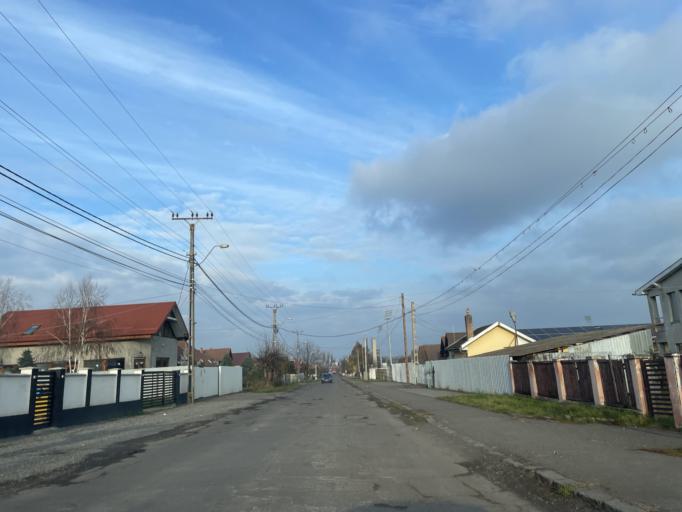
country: RO
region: Mures
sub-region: Municipiul Reghin
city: Apalina
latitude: 46.7646
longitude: 24.6938
